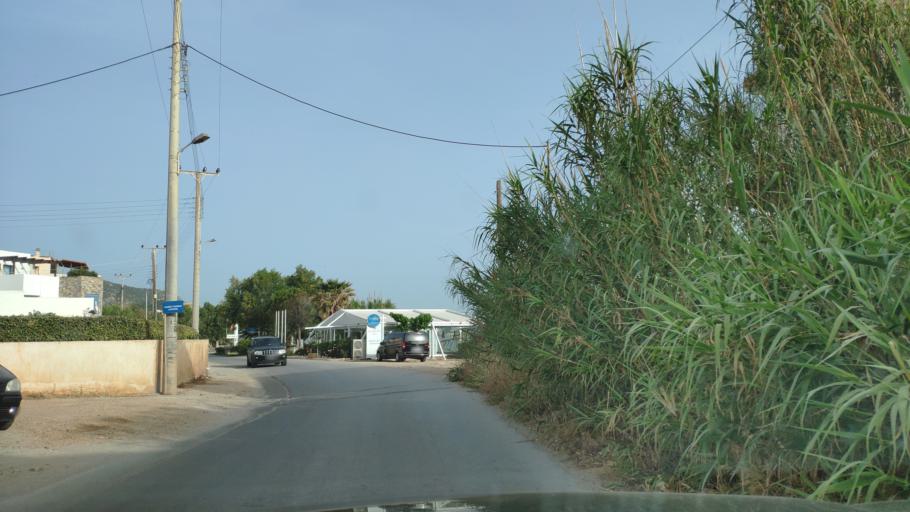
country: GR
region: Attica
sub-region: Nomarchia Anatolikis Attikis
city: Limin Mesoyaias
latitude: 37.8685
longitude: 24.0311
